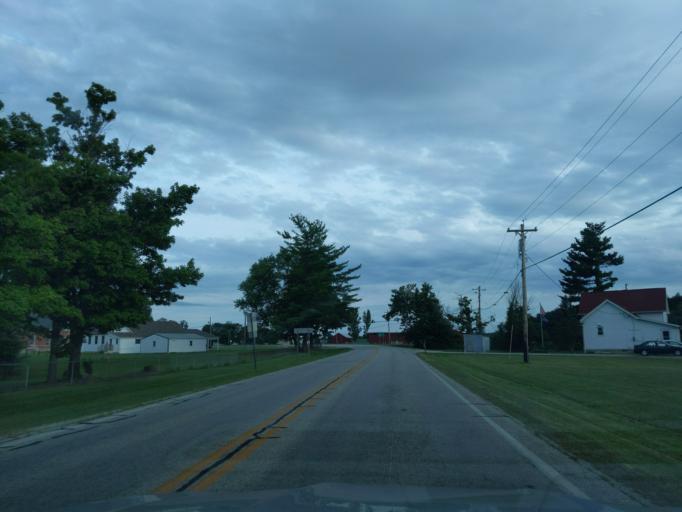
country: US
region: Indiana
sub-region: Ripley County
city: Sunman
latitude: 39.2710
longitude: -85.0975
